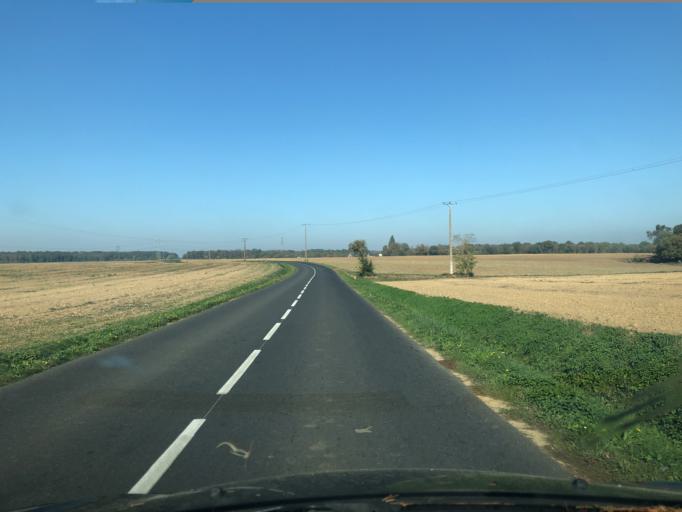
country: FR
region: Centre
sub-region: Departement d'Indre-et-Loire
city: Rouziers-de-Touraine
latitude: 47.5220
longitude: 0.6454
